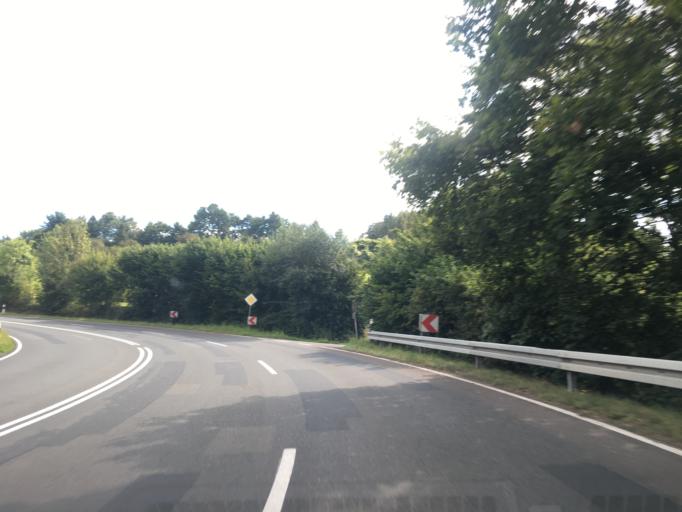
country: DE
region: Lower Saxony
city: Bad Pyrmont
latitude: 51.9855
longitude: 9.2158
